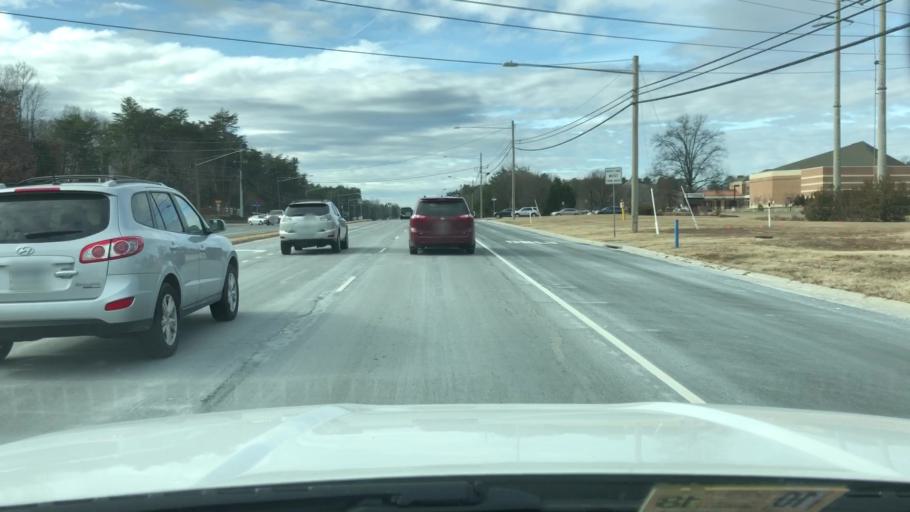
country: US
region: Virginia
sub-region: Fairfax County
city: Centreville
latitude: 38.8325
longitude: -77.4671
